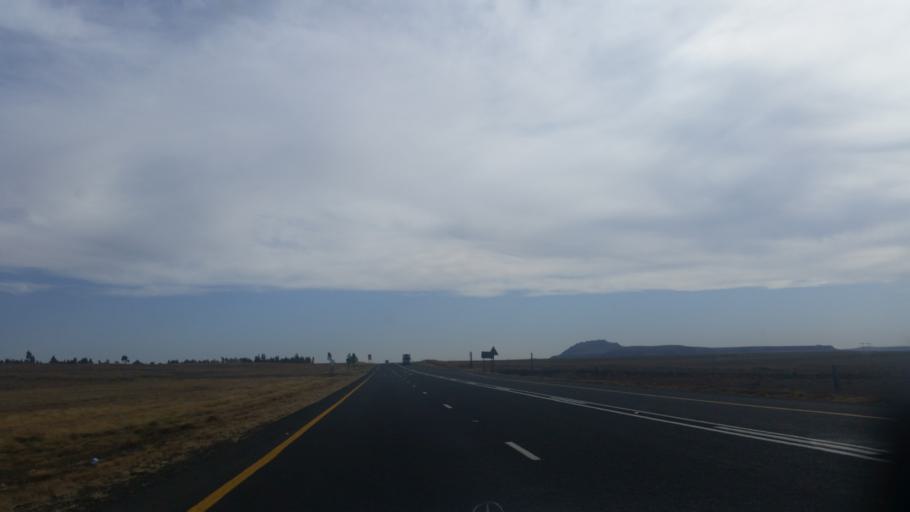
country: ZA
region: Orange Free State
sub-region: Thabo Mofutsanyana District Municipality
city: Phuthaditjhaba
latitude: -28.2747
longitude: 28.8475
